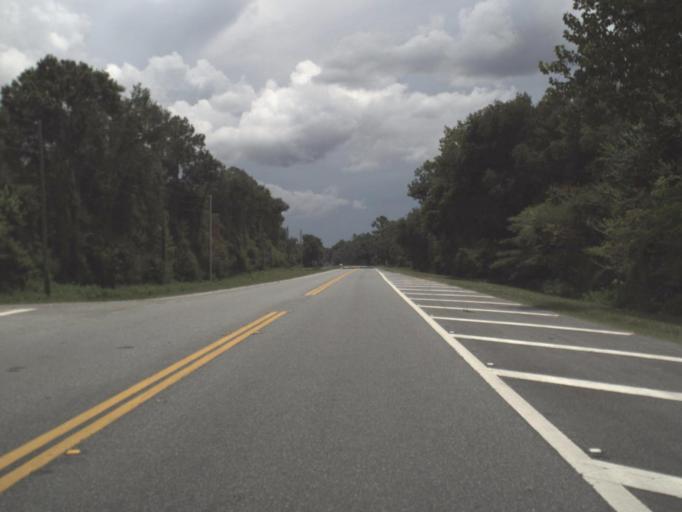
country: US
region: Florida
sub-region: Taylor County
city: Perry
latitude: 30.0874
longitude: -83.5305
